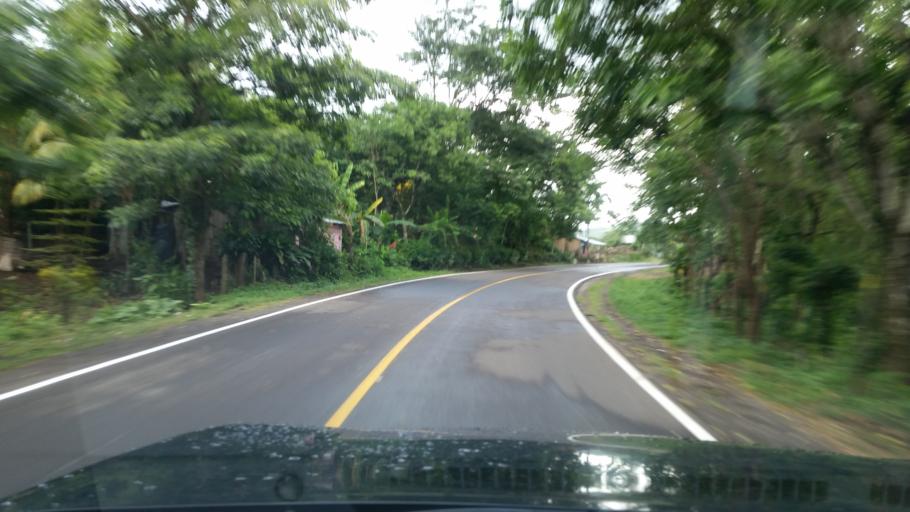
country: NI
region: Matagalpa
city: San Ramon
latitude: 13.0535
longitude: -85.7561
